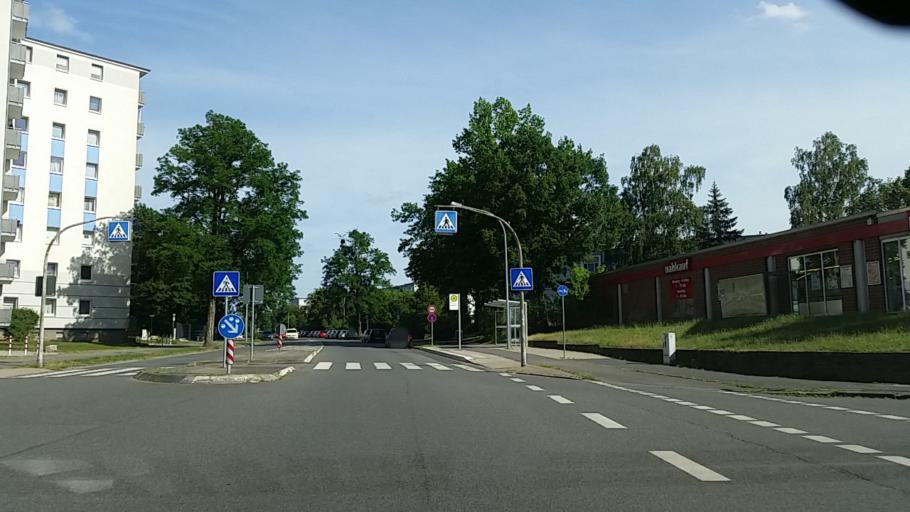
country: DE
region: Lower Saxony
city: Wolfsburg
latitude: 52.4123
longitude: 10.7629
